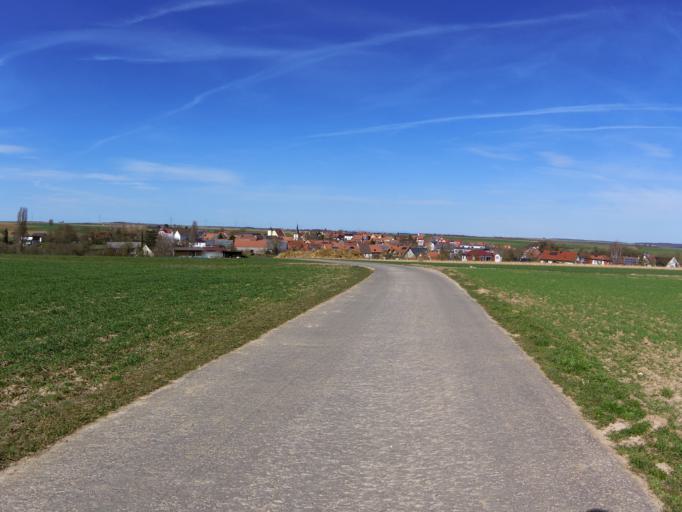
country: DE
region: Bavaria
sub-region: Regierungsbezirk Unterfranken
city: Biebelried
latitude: 49.7924
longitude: 10.1080
